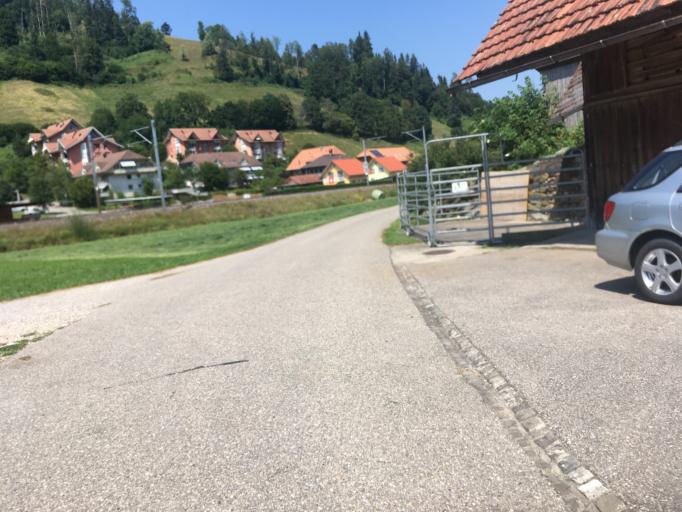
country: CH
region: Bern
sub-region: Emmental District
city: Signau
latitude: 46.9152
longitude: 7.7207
